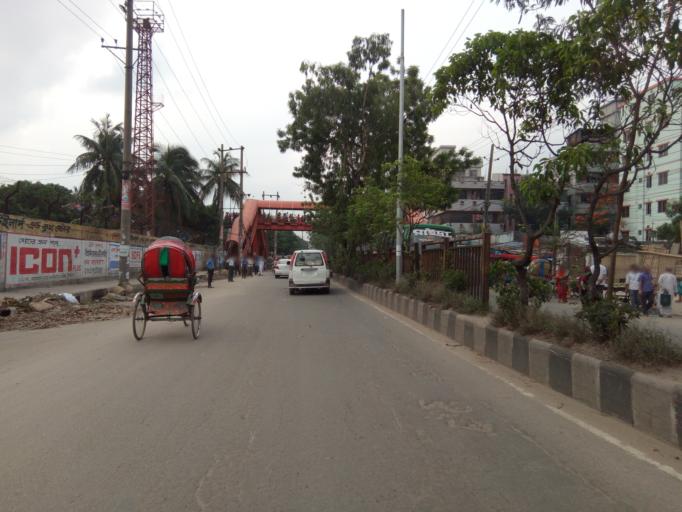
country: BD
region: Dhaka
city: Paltan
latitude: 23.7319
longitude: 90.4285
